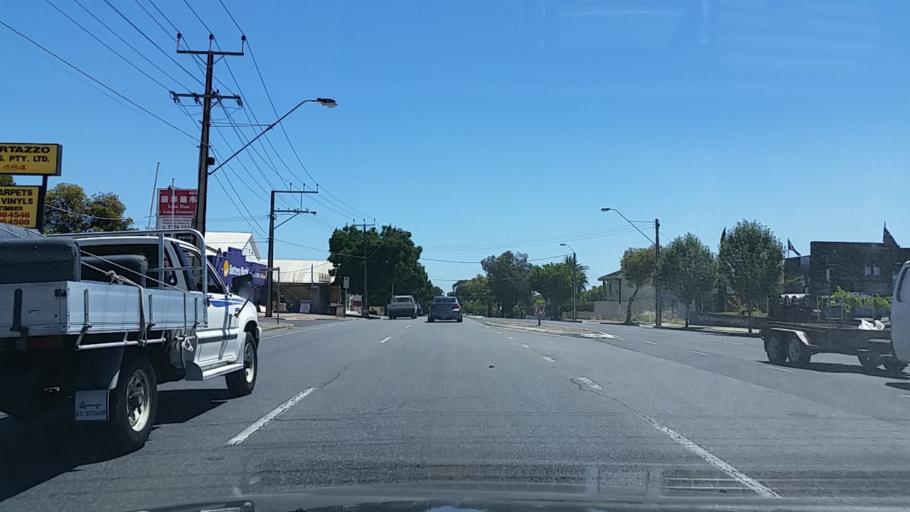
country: AU
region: South Australia
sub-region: Campbelltown
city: Hectorville
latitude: -34.8906
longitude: 138.6537
